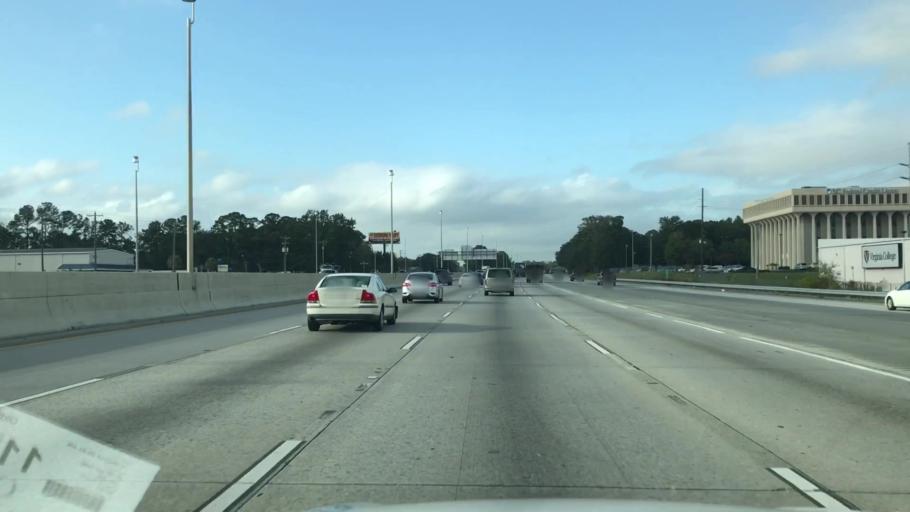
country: US
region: South Carolina
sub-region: Berkeley County
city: Hanahan
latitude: 32.9059
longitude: -80.0251
